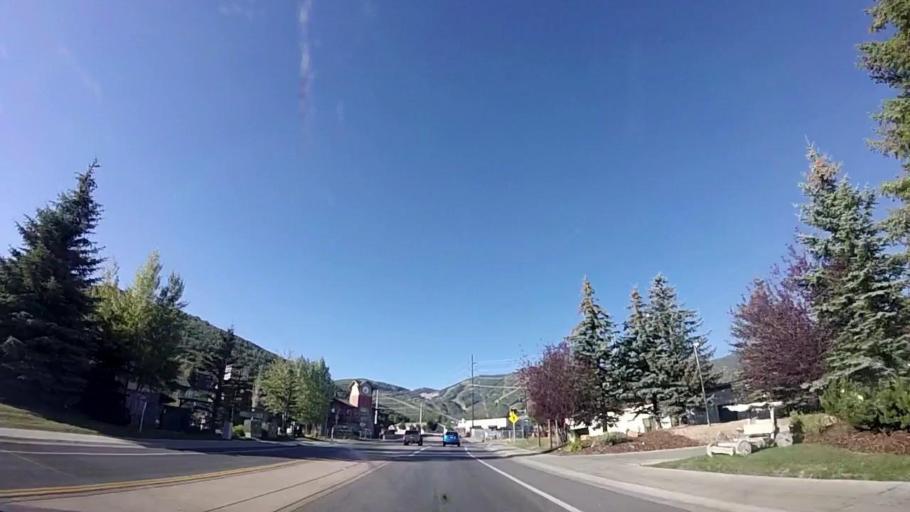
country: US
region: Utah
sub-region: Summit County
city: Park City
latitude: 40.6612
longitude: -111.5013
